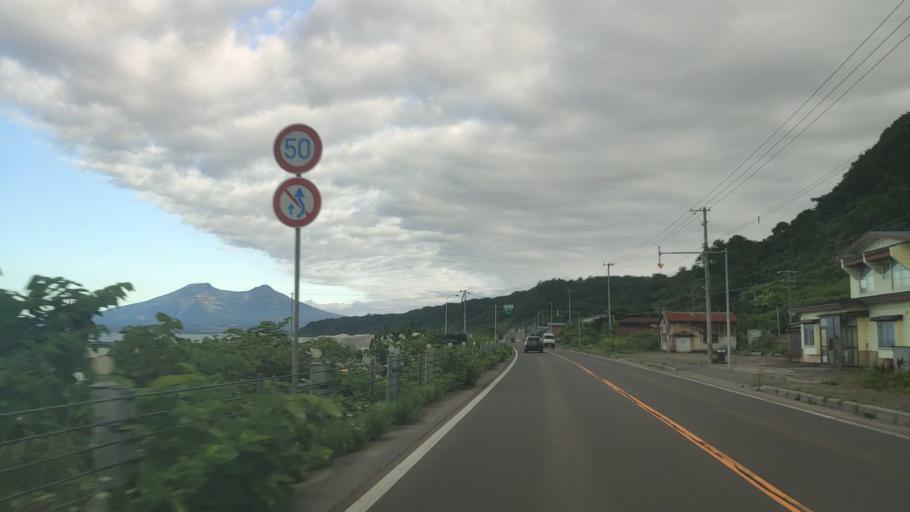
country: JP
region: Hokkaido
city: Nanae
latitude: 42.1333
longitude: 140.5093
